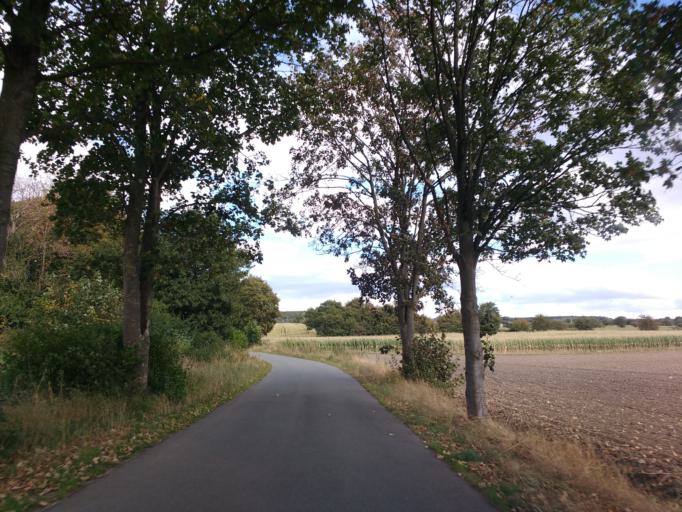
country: DE
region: North Rhine-Westphalia
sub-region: Regierungsbezirk Detmold
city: Schlangen
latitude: 51.7913
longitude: 8.8529
